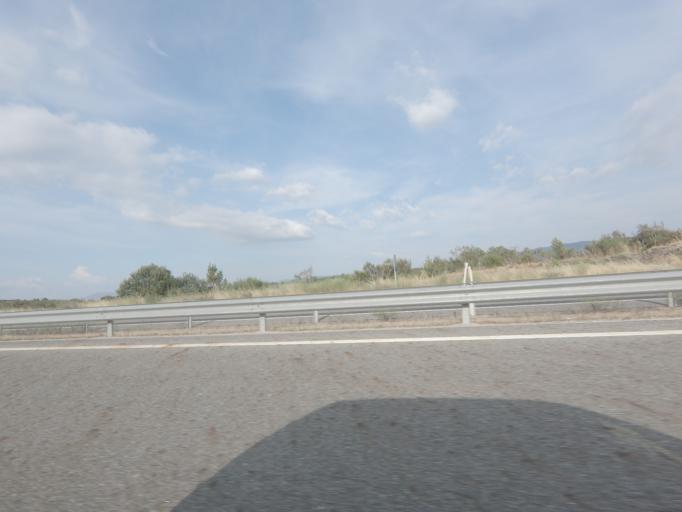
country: PT
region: Vila Real
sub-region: Chaves
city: Chaves
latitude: 41.7406
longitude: -7.5249
